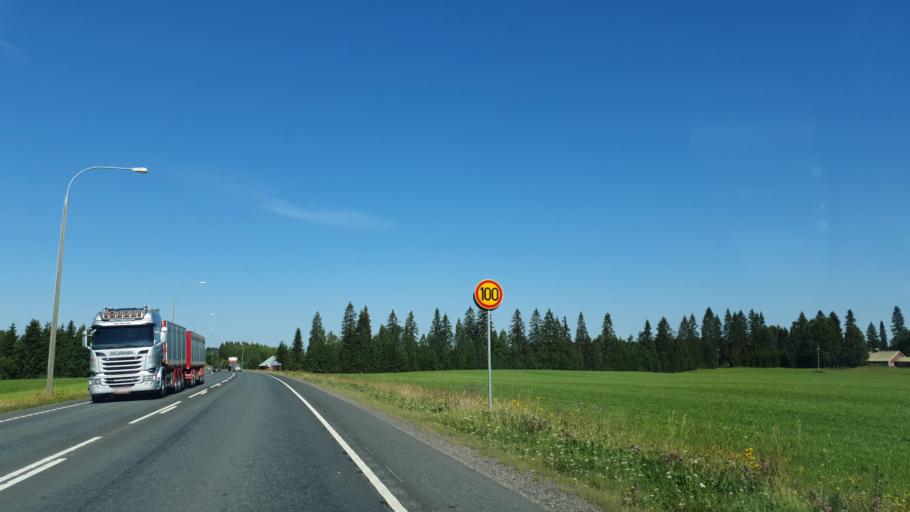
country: FI
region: Northern Savo
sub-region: Kuopio
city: Siilinjaervi
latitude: 63.2109
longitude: 27.5310
